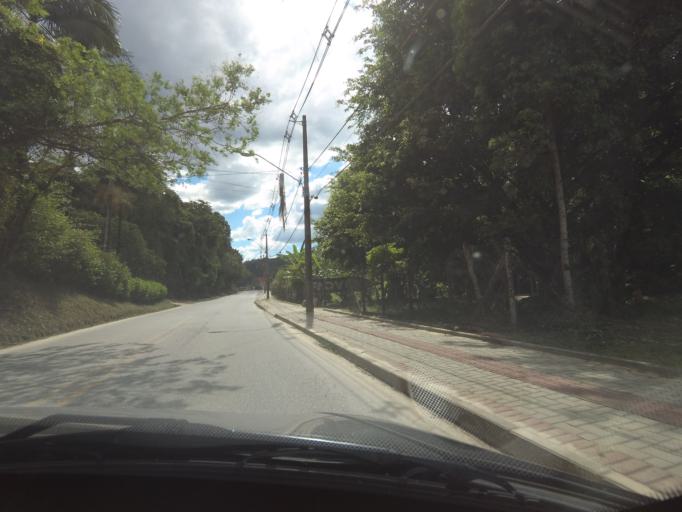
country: BR
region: Santa Catarina
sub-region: Brusque
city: Brusque
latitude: -27.0710
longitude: -48.9399
